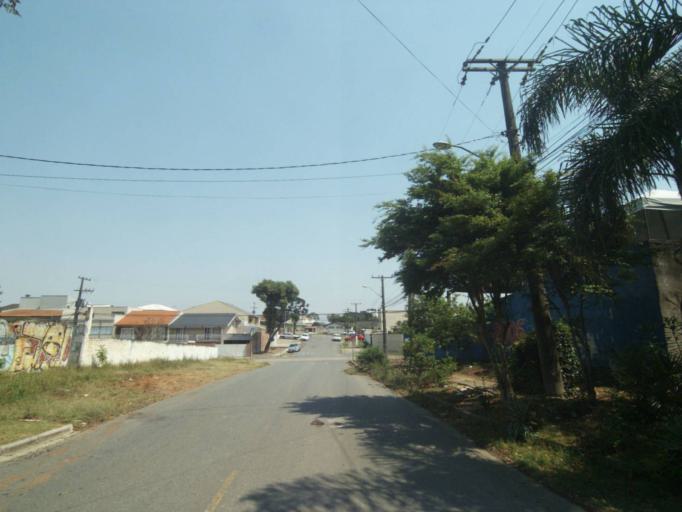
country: BR
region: Parana
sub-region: Sao Jose Dos Pinhais
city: Sao Jose dos Pinhais
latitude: -25.4994
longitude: -49.2716
